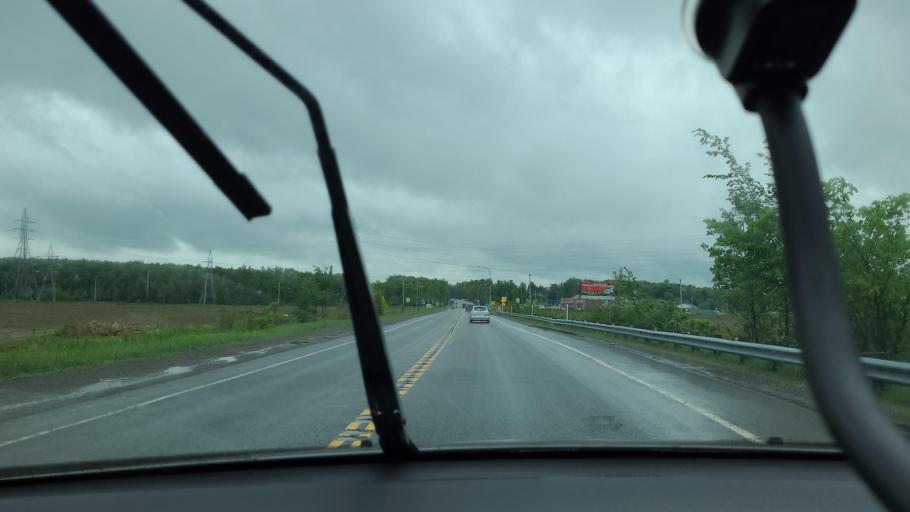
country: CA
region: Quebec
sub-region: Laurentides
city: Saint-Colomban
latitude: 45.7223
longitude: -74.0750
